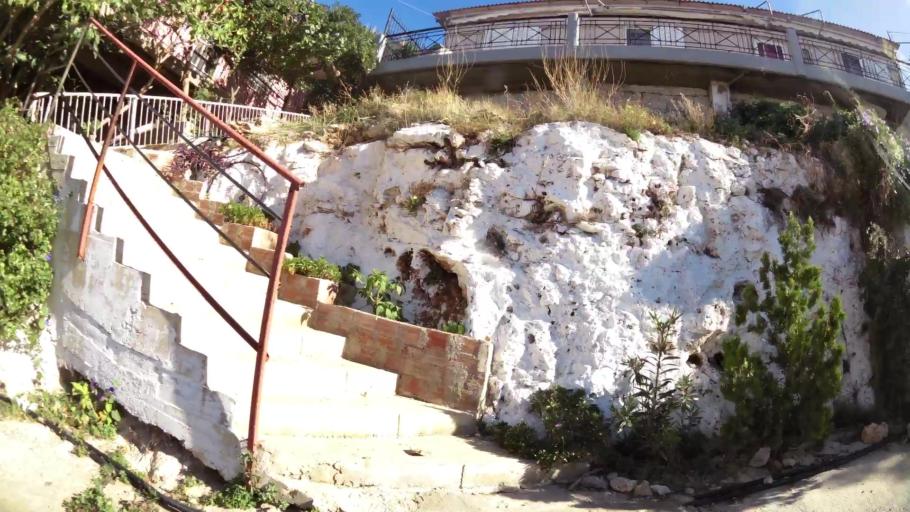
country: GR
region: Attica
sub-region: Nomos Piraios
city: Perama
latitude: 37.9649
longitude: 23.5930
